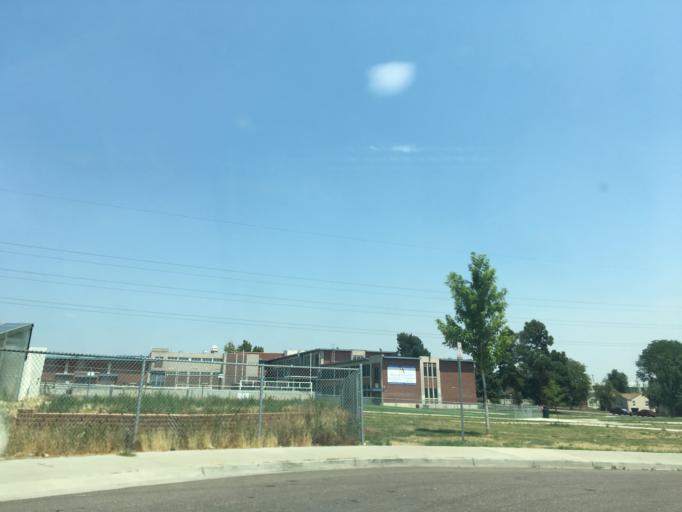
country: US
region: Colorado
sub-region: Arapahoe County
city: Sheridan
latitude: 39.6980
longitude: -105.0285
